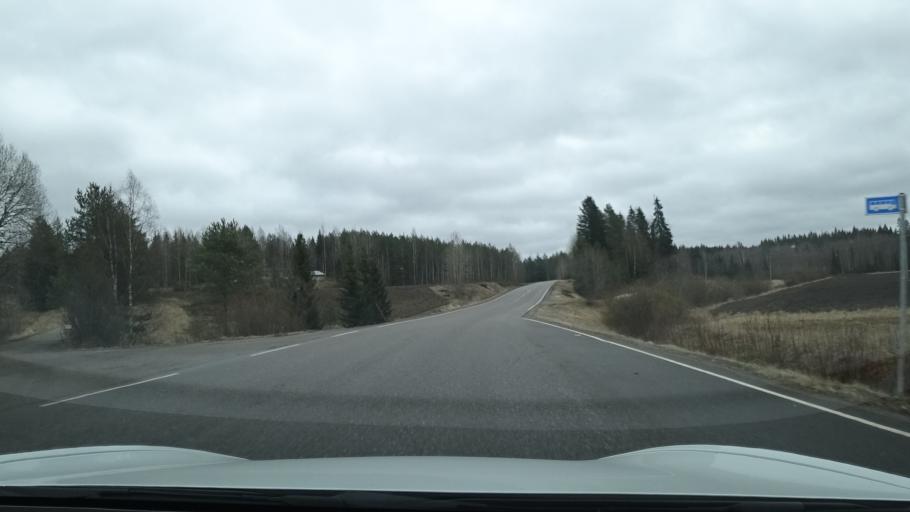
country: FI
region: Uusimaa
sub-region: Helsinki
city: Pornainen
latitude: 60.4865
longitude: 25.4204
